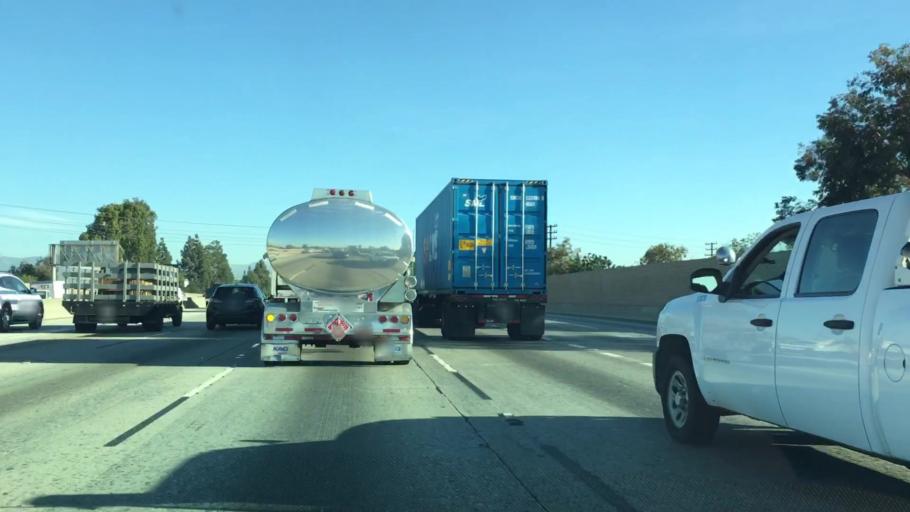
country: US
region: California
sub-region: Los Angeles County
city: Santa Fe Springs
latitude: 33.9314
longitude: -118.1014
